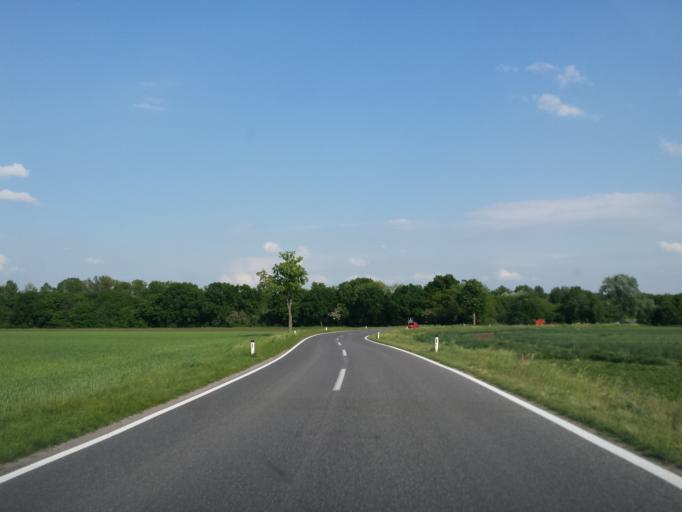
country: AT
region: Lower Austria
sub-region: Politischer Bezirk Ganserndorf
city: Marchegg
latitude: 48.2907
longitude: 16.8799
